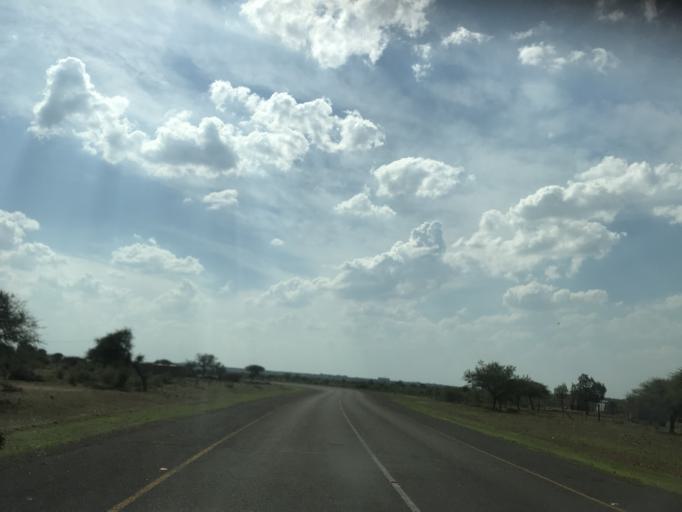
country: BW
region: South East
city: Janeng
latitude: -25.4943
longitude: 25.6401
